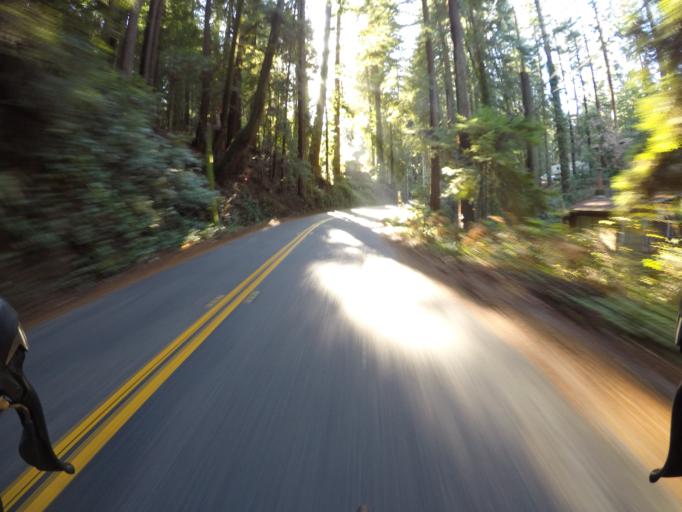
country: US
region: California
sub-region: Santa Cruz County
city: Felton
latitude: 37.0365
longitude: -122.0731
